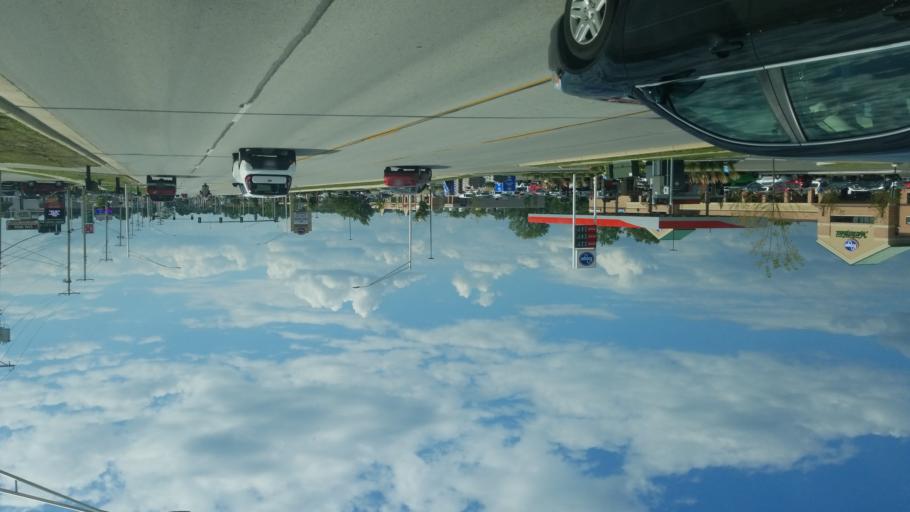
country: US
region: Ohio
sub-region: Wood County
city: Bowling Green
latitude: 41.3926
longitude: -83.6506
